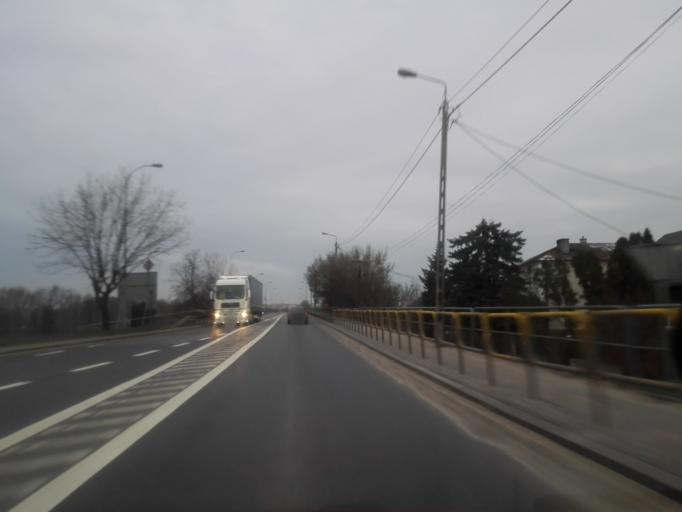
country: PL
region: Podlasie
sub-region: Powiat lomzynski
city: Piatnica
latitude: 53.1946
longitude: 22.0947
